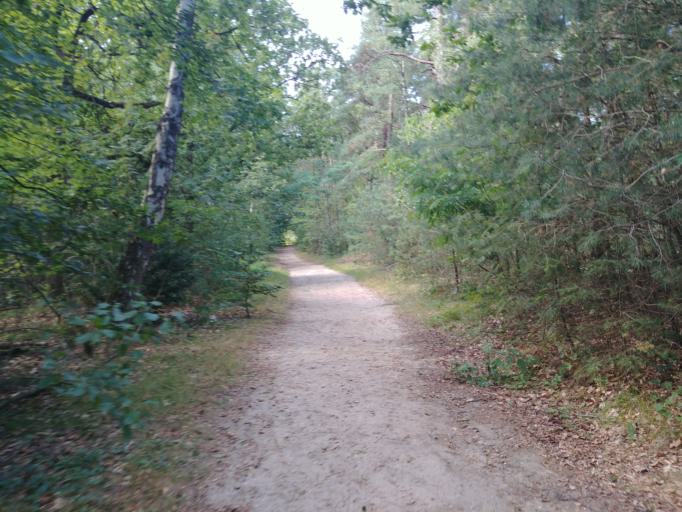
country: NL
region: Utrecht
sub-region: Gemeente Utrechtse Heuvelrug
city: Doorn
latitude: 52.0443
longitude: 5.3570
